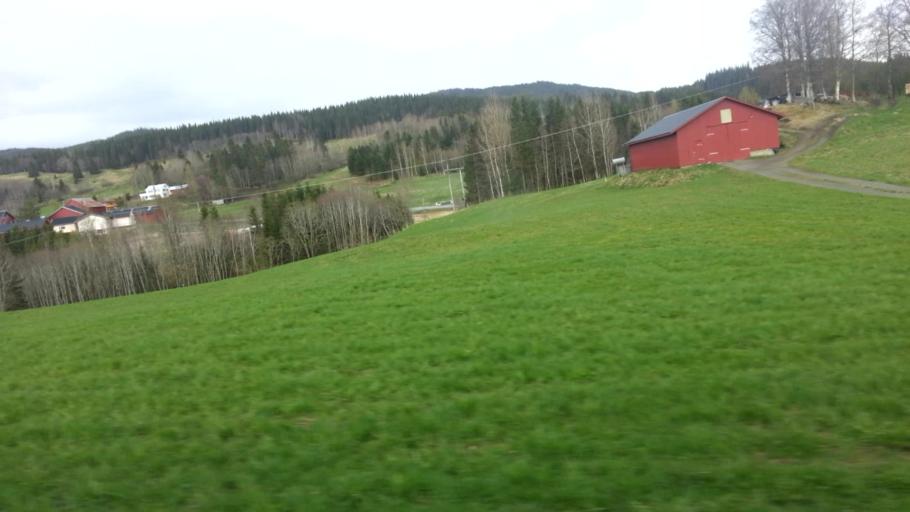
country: NO
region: Nord-Trondelag
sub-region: Levanger
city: Skogn
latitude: 63.6576
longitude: 11.2363
